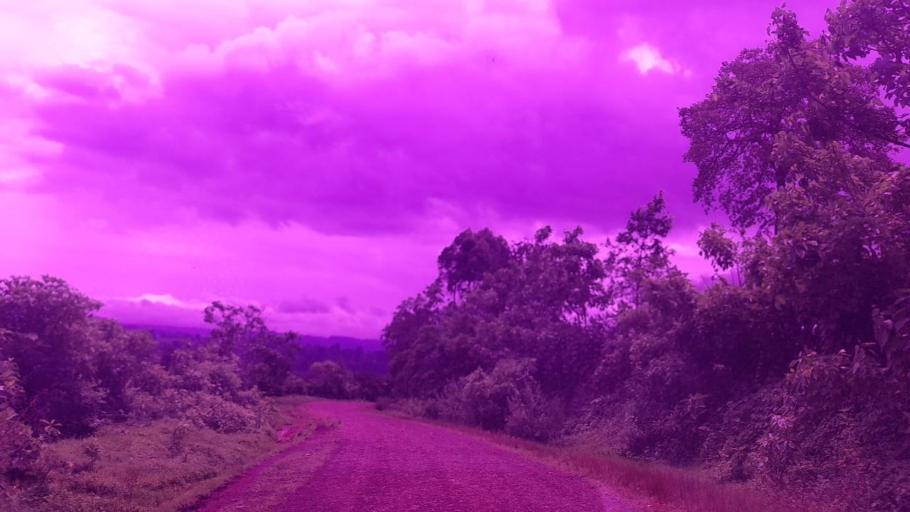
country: ET
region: Southern Nations, Nationalities, and People's Region
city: Tippi
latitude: 7.6315
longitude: 35.5736
